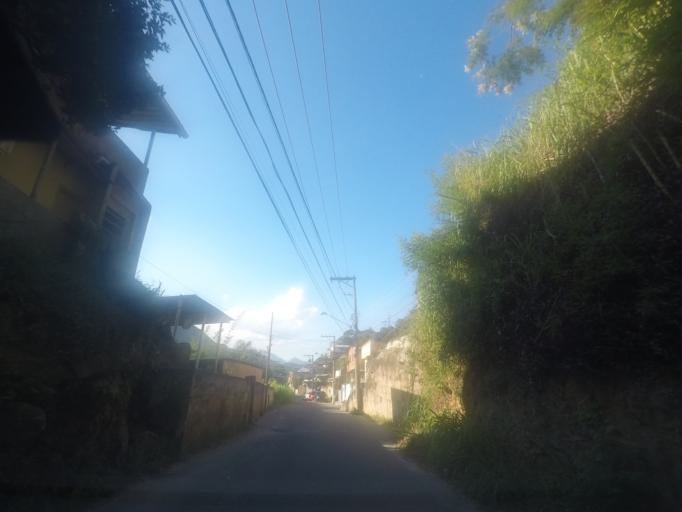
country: BR
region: Rio de Janeiro
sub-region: Petropolis
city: Petropolis
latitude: -22.4950
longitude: -43.1490
